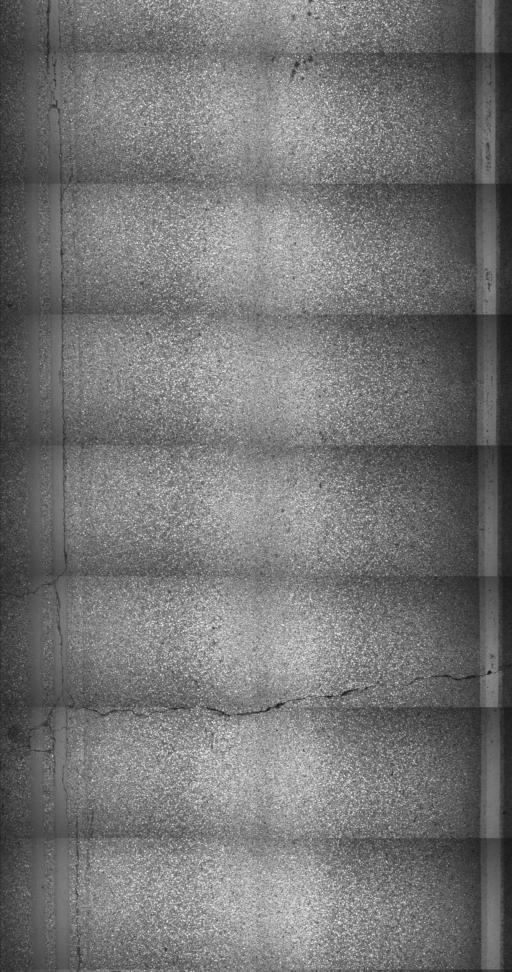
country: US
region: Vermont
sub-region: Orange County
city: Randolph
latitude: 43.7982
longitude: -72.7696
